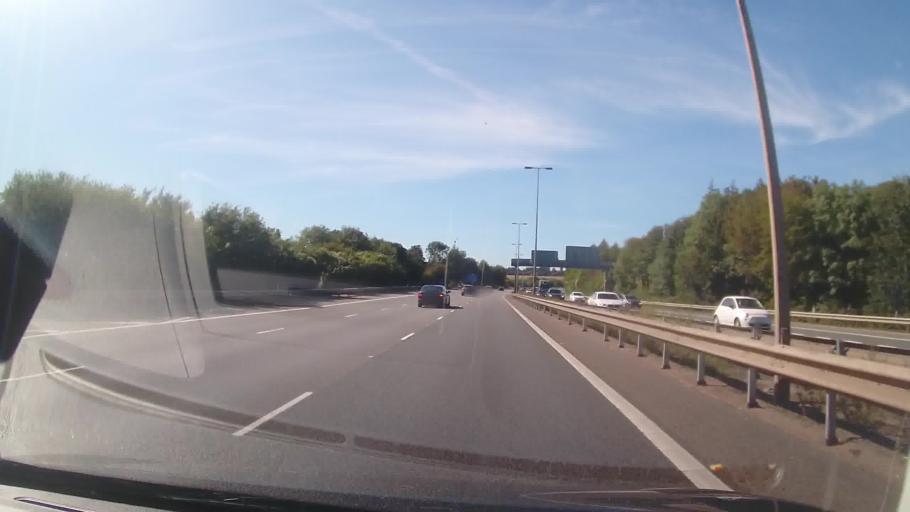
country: GB
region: England
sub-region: Buckinghamshire
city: High Wycombe
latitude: 51.6104
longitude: -0.7781
